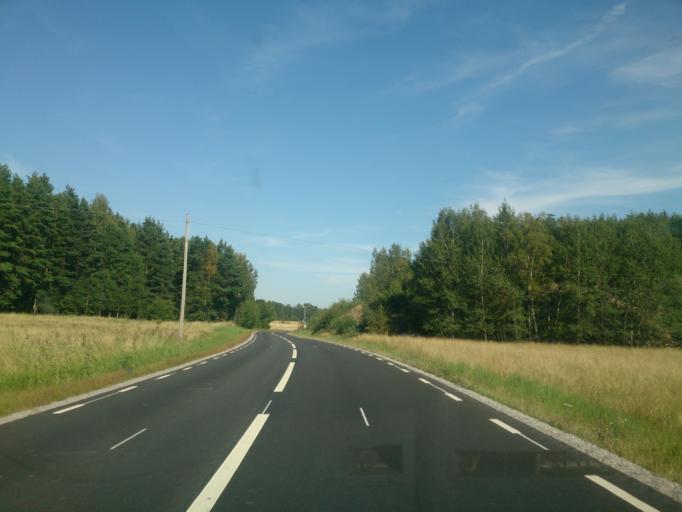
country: SE
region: OEstergoetland
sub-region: Norrkopings Kommun
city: Krokek
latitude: 58.5747
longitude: 16.5105
